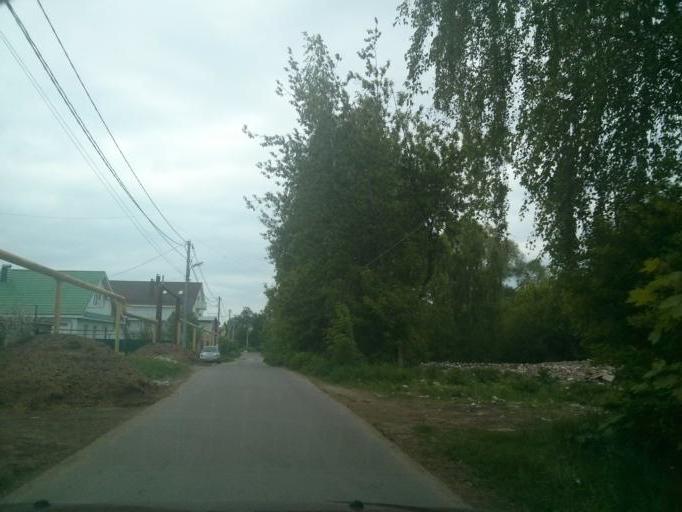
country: RU
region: Nizjnij Novgorod
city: Afonino
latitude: 56.3036
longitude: 44.0980
